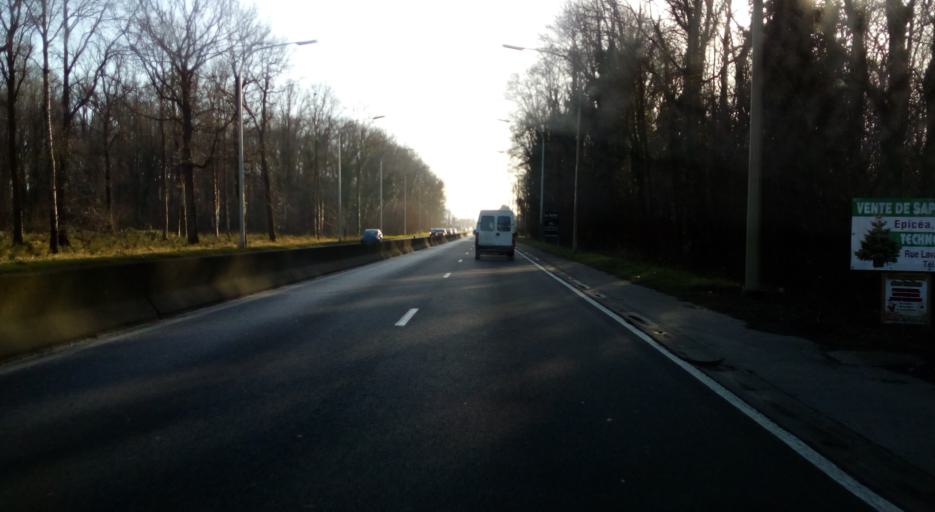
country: BE
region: Wallonia
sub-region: Province du Hainaut
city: Gerpinnes
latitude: 50.3494
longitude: 4.4721
